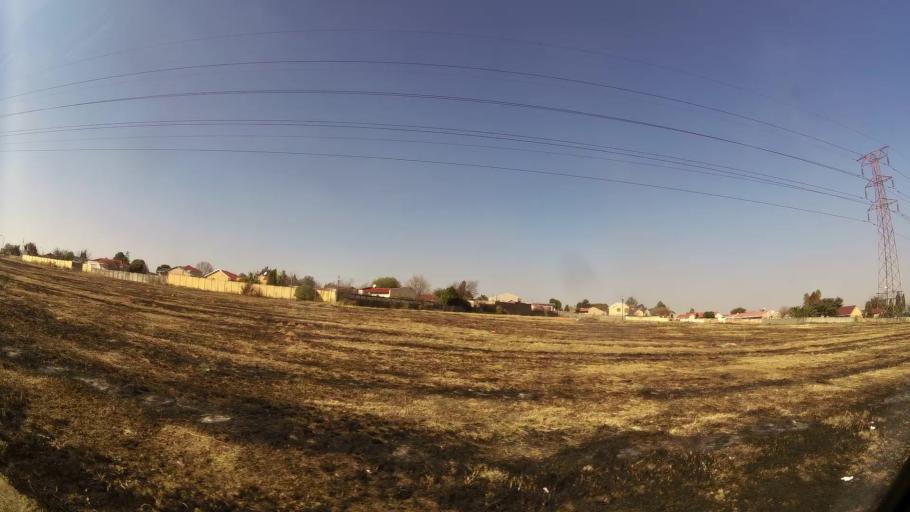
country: ZA
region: Gauteng
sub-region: City of Johannesburg Metropolitan Municipality
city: Johannesburg
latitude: -26.2590
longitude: 27.9907
